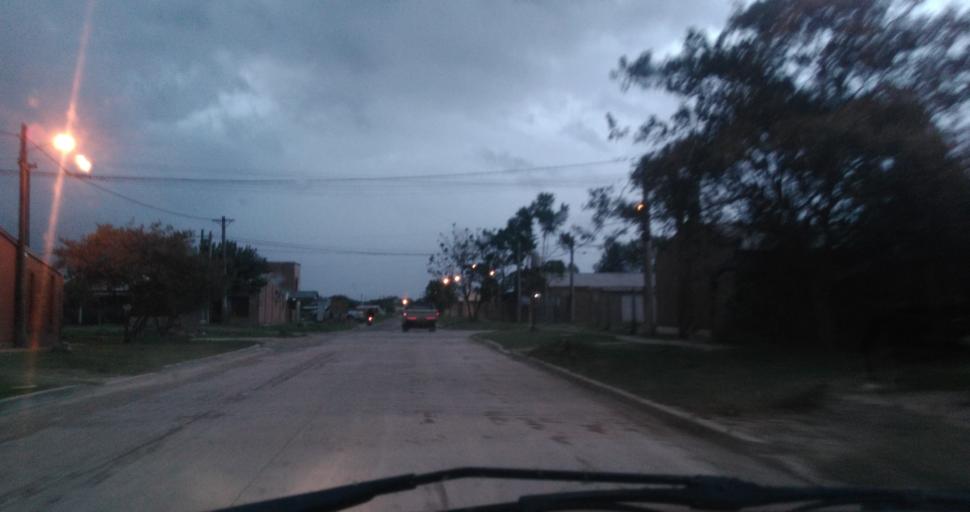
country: AR
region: Chaco
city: Fontana
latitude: -27.4182
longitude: -59.0464
